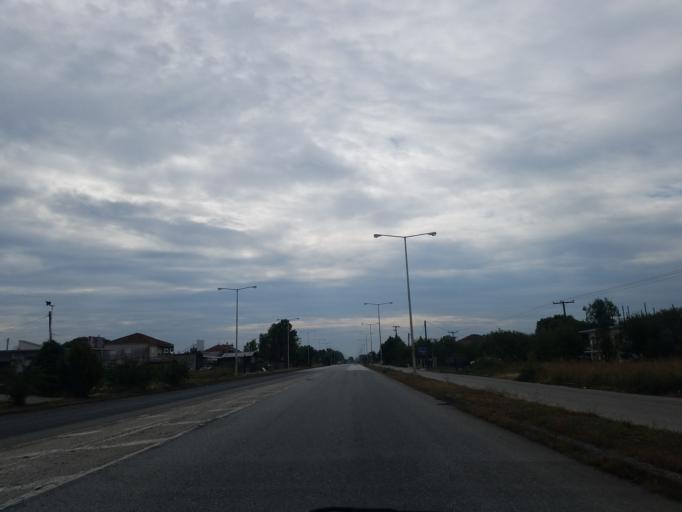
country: GR
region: Thessaly
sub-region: Trikala
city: Pyrgetos
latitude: 39.5841
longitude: 21.7396
